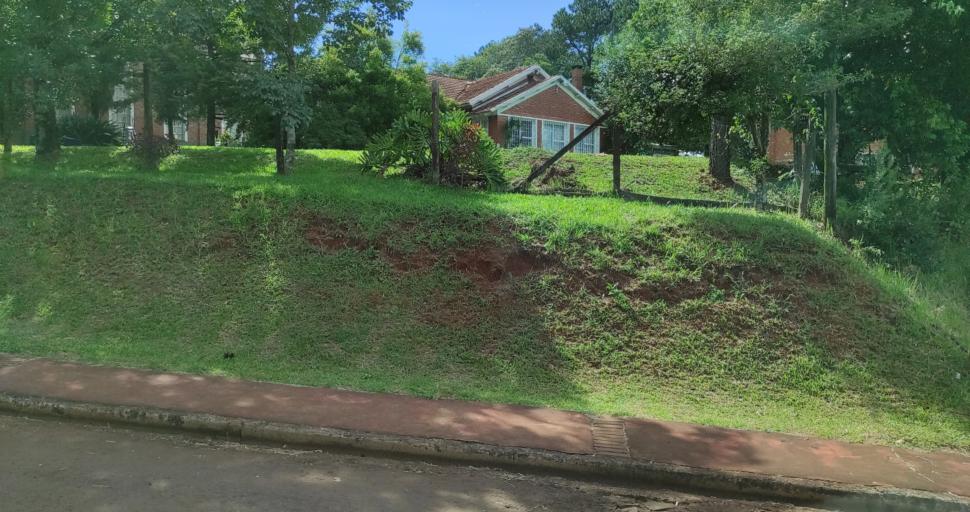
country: AR
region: Misiones
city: Dos de Mayo
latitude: -27.0182
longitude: -54.6865
